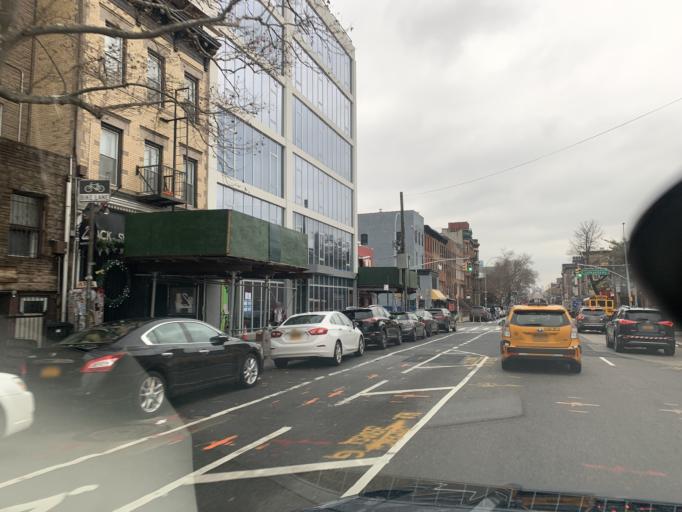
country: US
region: New York
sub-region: Kings County
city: Brooklyn
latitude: 40.6890
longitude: -73.9550
